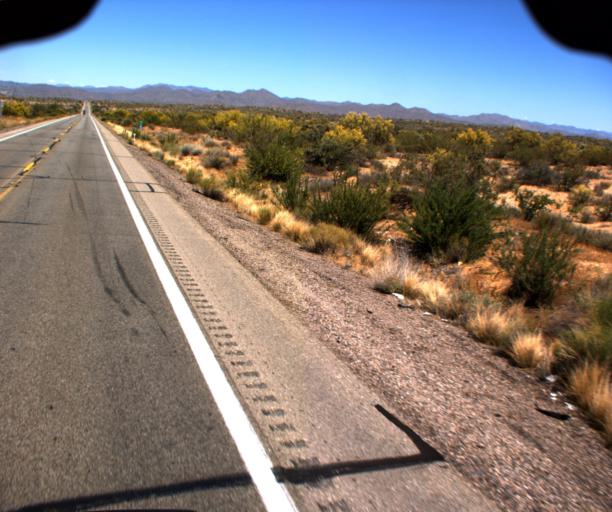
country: US
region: Arizona
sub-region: Yavapai County
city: Bagdad
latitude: 34.3225
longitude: -113.1363
